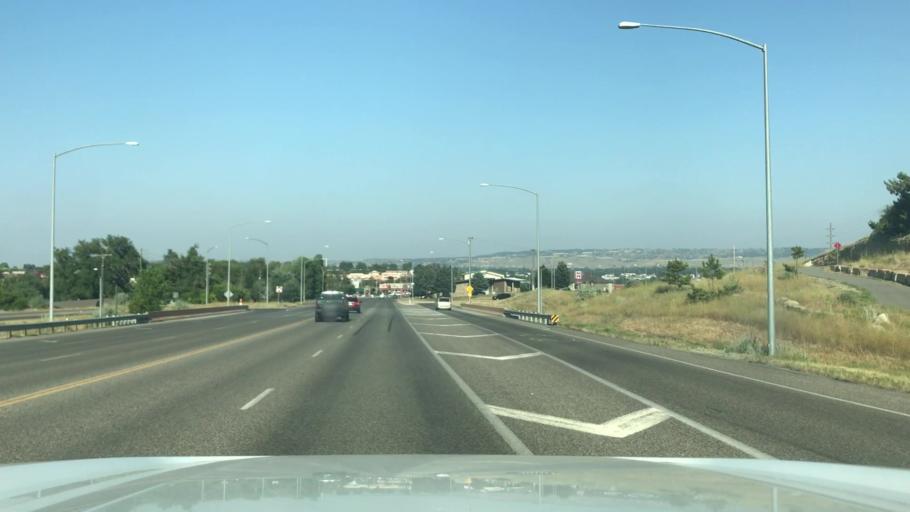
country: US
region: Montana
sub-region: Yellowstone County
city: Billings
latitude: 45.8028
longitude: -108.4843
